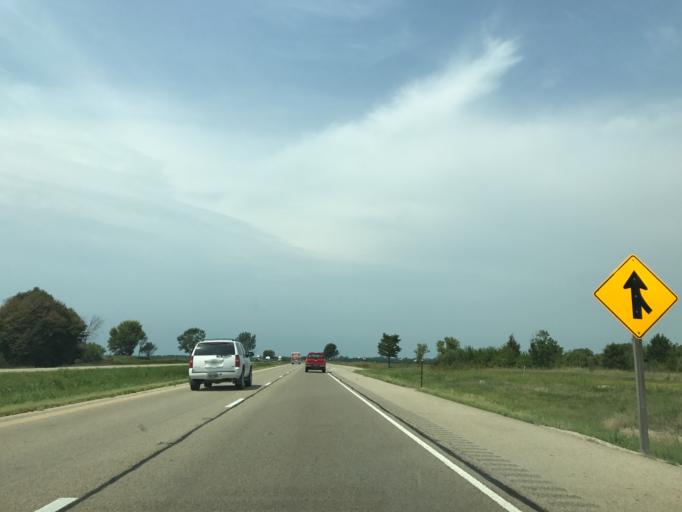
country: US
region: Illinois
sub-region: Bureau County
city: Ladd
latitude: 41.3681
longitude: -89.2210
